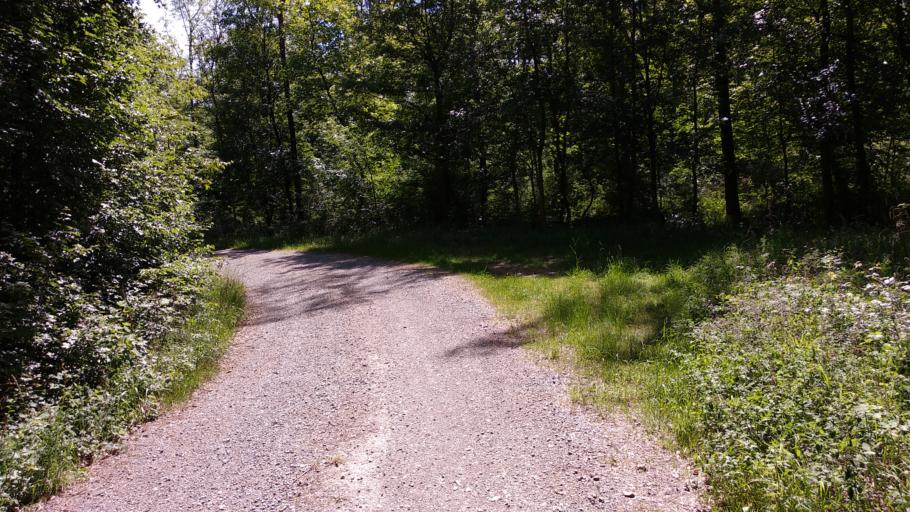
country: DE
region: North Rhine-Westphalia
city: Beverungen
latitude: 51.6430
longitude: 9.3537
